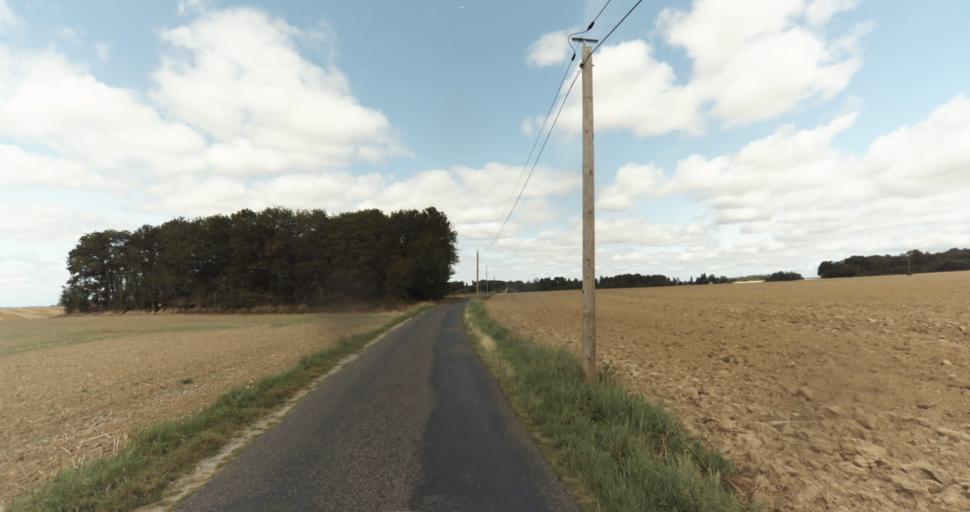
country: FR
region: Haute-Normandie
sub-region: Departement de l'Eure
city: Evreux
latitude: 48.9259
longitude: 1.2486
